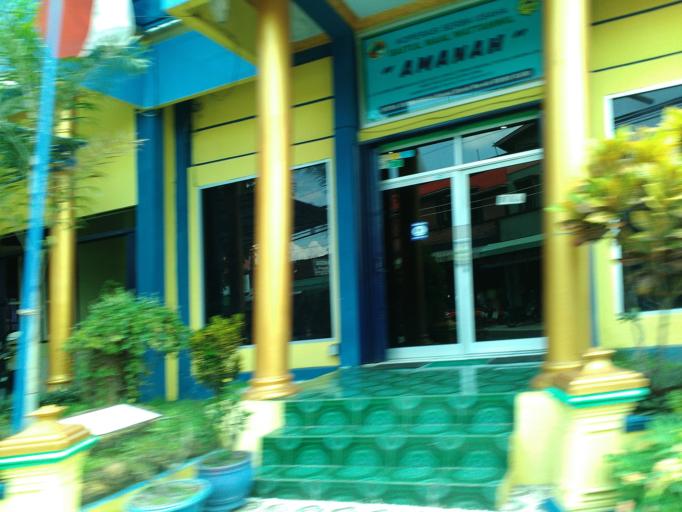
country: ID
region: Central Java
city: Klaten
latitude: -7.6904
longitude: 110.6119
